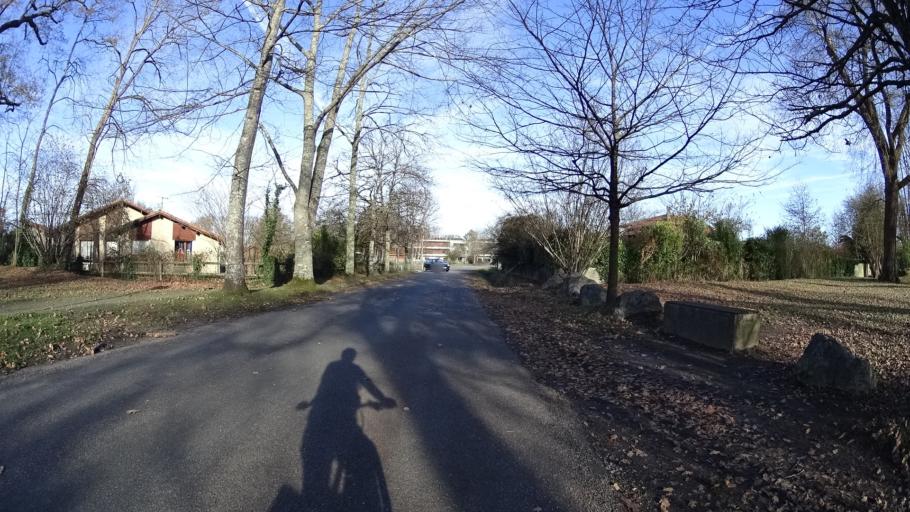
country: FR
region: Aquitaine
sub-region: Departement des Landes
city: Saint-Paul-les-Dax
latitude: 43.7330
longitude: -1.0586
